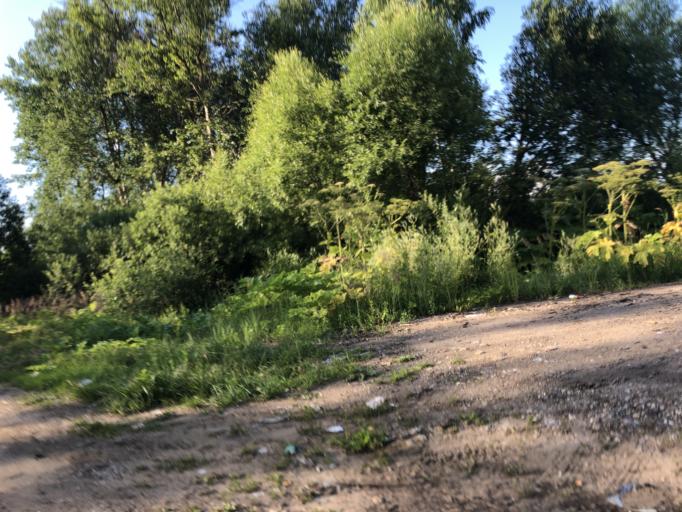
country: RU
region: Tverskaya
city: Rzhev
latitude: 56.2718
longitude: 34.2459
